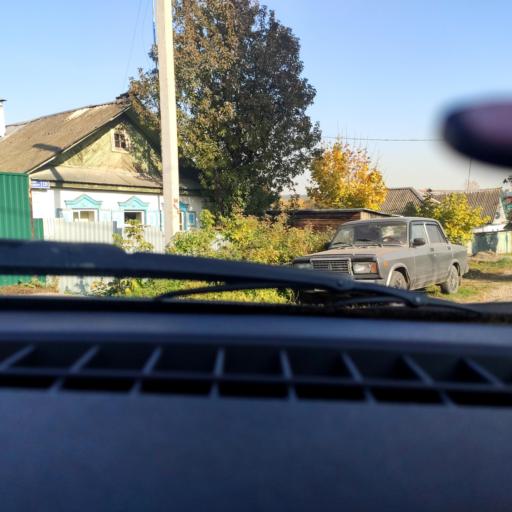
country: RU
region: Bashkortostan
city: Ufa
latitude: 54.8238
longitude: 56.1150
